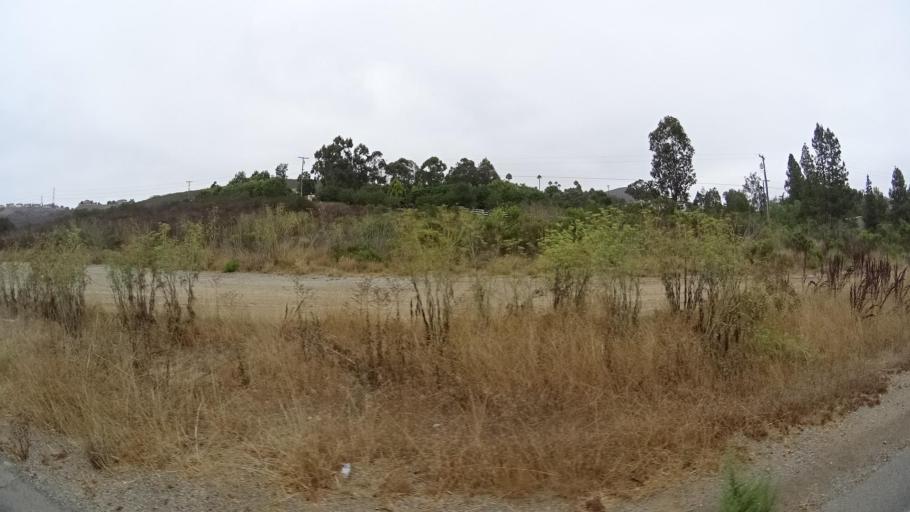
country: US
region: California
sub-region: San Diego County
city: Lake San Marcos
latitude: 33.0894
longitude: -117.1893
